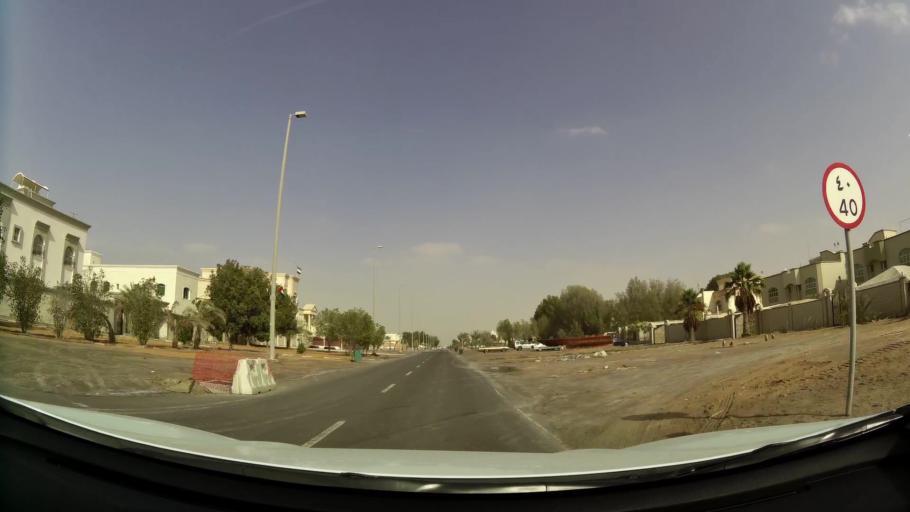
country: AE
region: Abu Dhabi
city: Abu Dhabi
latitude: 24.4113
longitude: 54.5798
